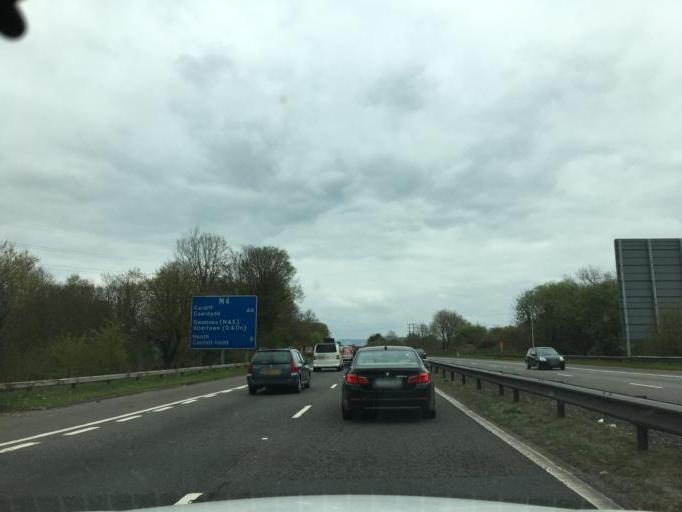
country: GB
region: Wales
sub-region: City and County of Swansea
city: Morriston
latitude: 51.6769
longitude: -3.9485
